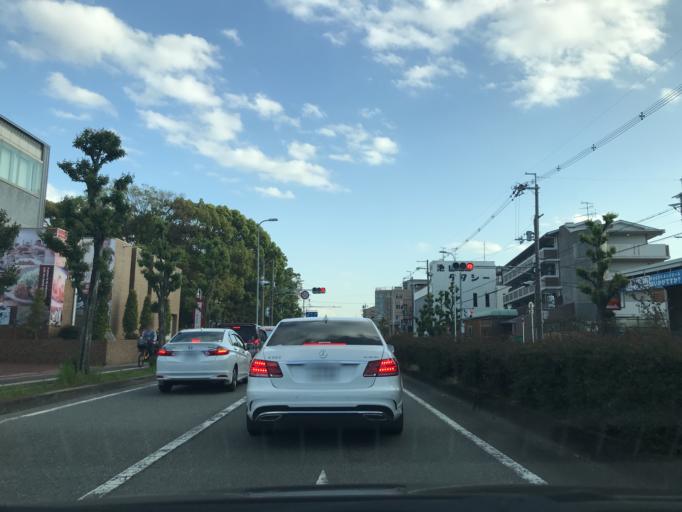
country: JP
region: Osaka
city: Ikeda
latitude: 34.8095
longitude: 135.4401
